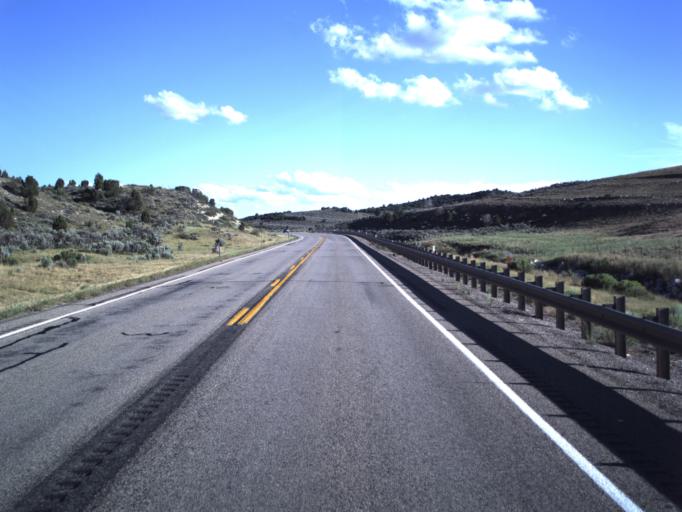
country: US
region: Utah
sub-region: Sanpete County
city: Fairview
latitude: 39.7369
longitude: -111.4771
